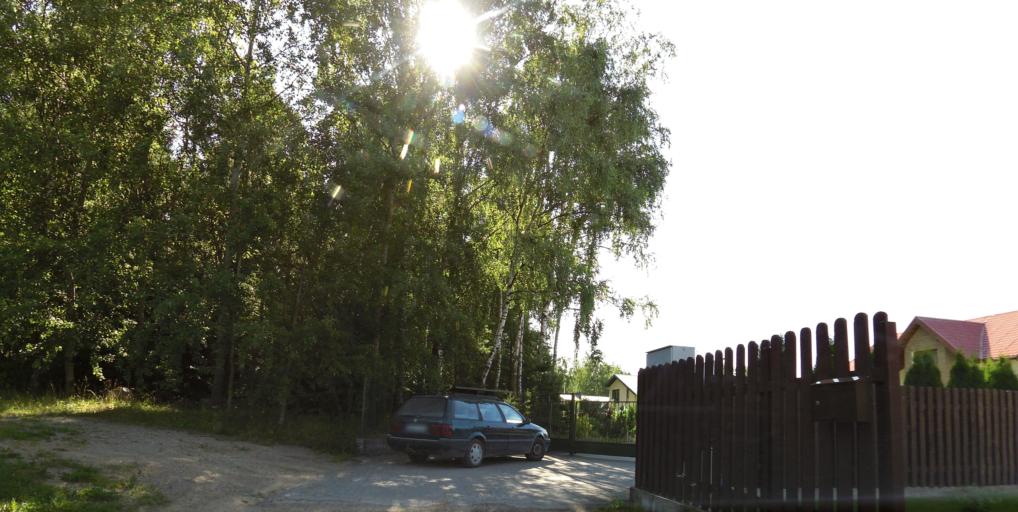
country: LT
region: Vilnius County
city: Pilaite
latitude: 54.6894
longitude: 25.1811
